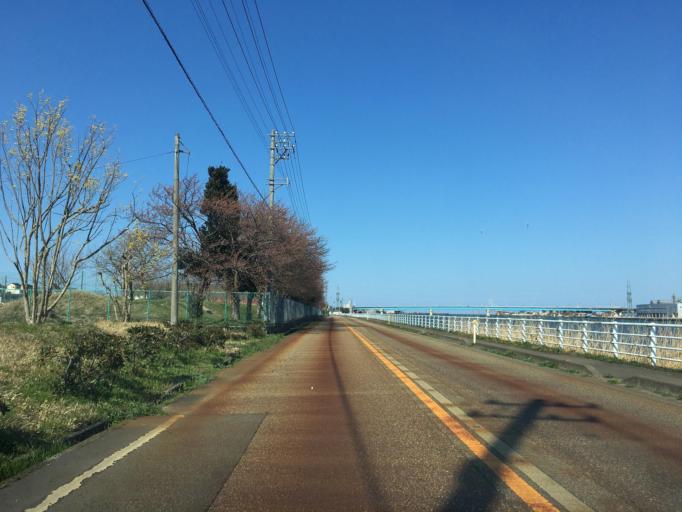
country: JP
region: Toyama
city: Nishishinminato
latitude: 36.7836
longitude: 137.0511
